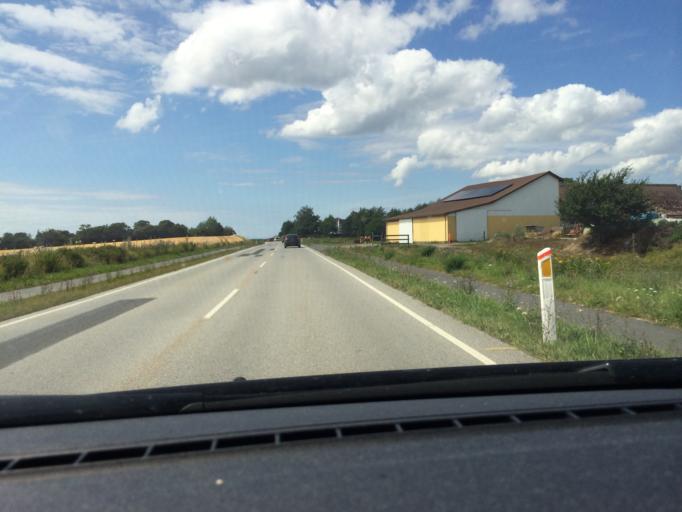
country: DK
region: Zealand
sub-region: Vordingborg Kommune
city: Stege
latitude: 54.9951
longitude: 12.3167
